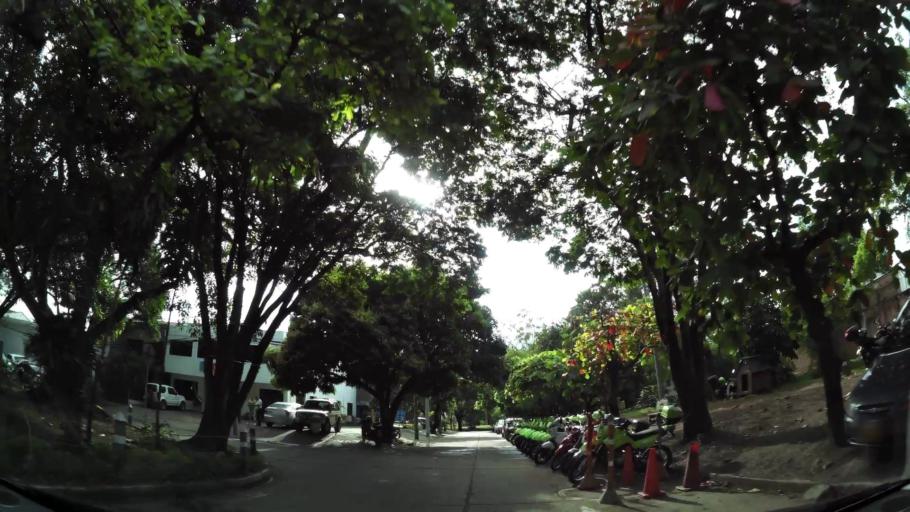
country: CO
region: Valle del Cauca
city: Cali
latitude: 3.4822
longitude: -76.5224
